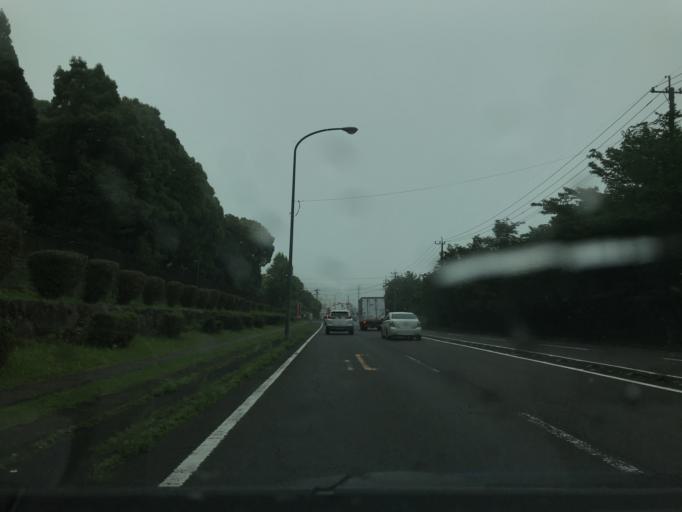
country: JP
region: Oita
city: Beppu
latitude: 33.2993
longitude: 131.4613
